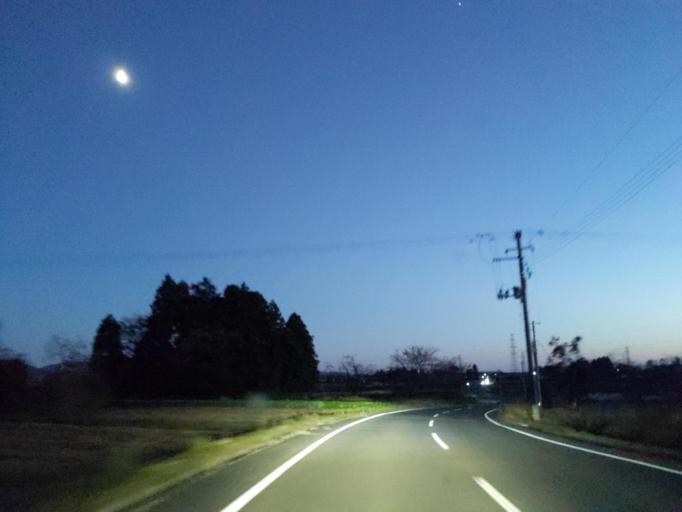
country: JP
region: Fukushima
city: Sukagawa
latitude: 37.3317
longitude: 140.3871
